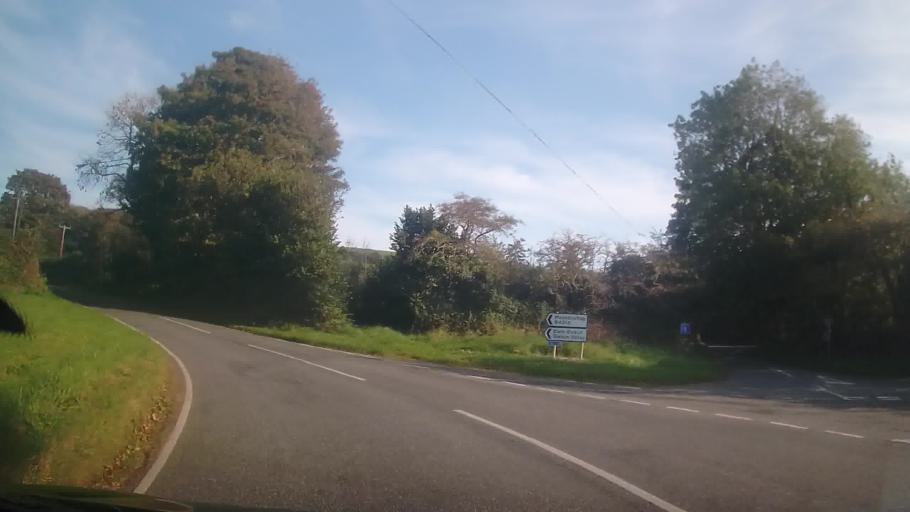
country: GB
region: Wales
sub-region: Pembrokeshire
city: Fishguard
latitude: 51.9758
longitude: -4.9254
